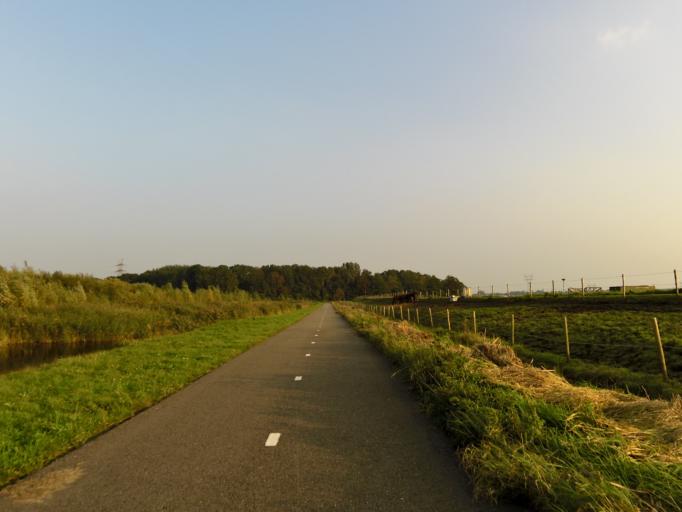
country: NL
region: South Holland
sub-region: Gemeente Rijnwoude
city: Benthuizen
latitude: 52.0601
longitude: 4.5618
